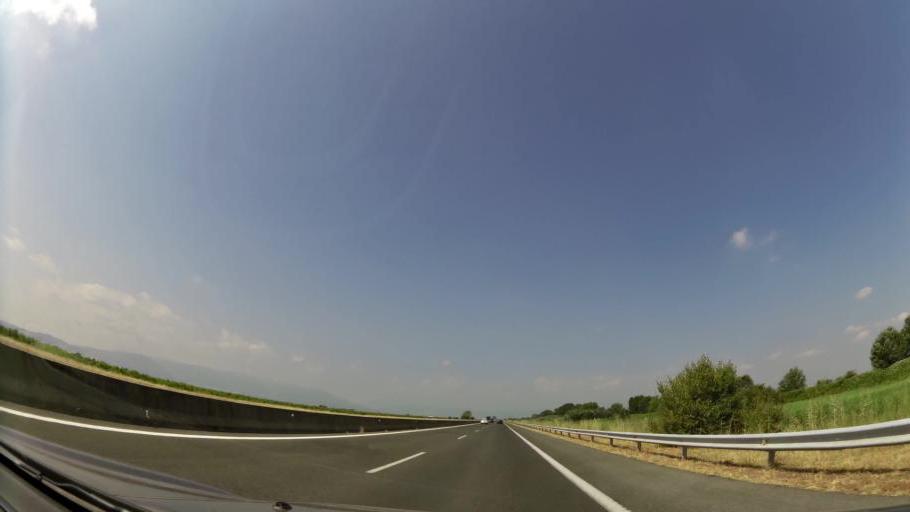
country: GR
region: Central Macedonia
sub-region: Nomos Imathias
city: Loutros
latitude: 40.5724
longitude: 22.3904
